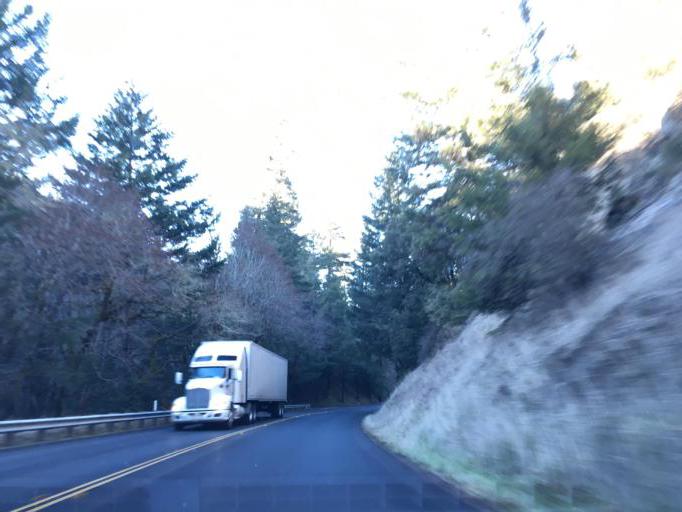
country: US
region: California
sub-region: Mendocino County
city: Laytonville
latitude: 39.8057
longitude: -123.5466
